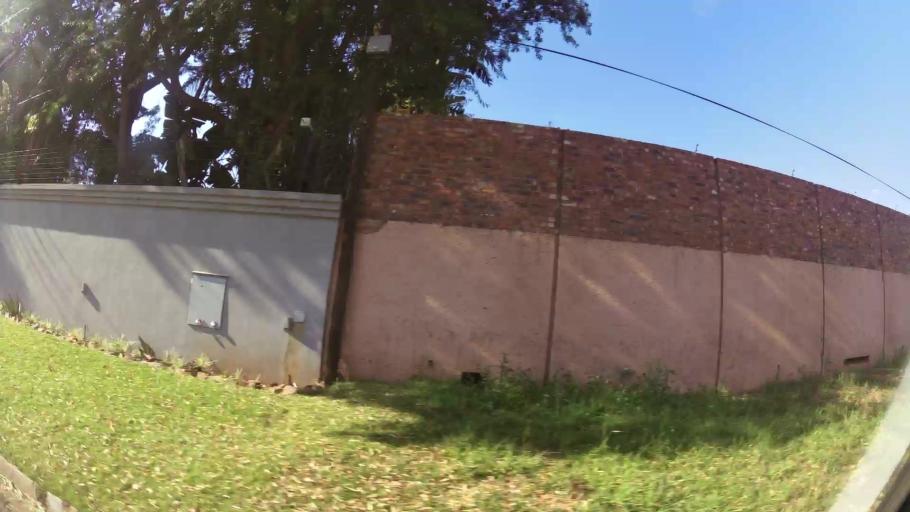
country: ZA
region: Gauteng
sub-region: Ekurhuleni Metropolitan Municipality
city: Germiston
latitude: -26.1783
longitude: 28.1472
